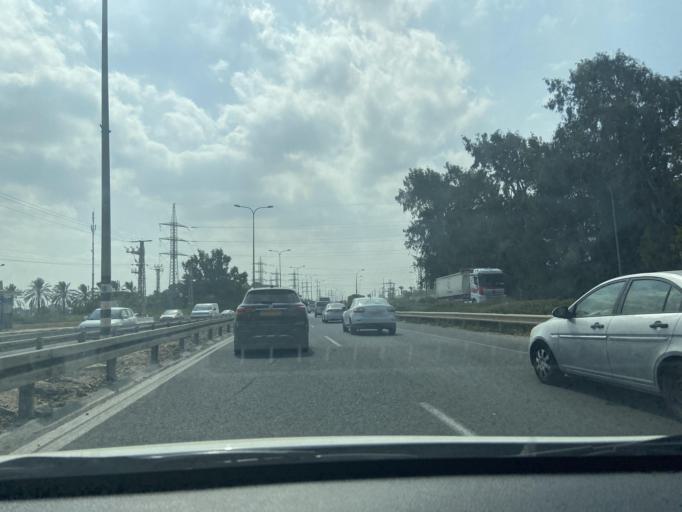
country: IL
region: Northern District
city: `Akko
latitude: 32.8975
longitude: 35.0931
